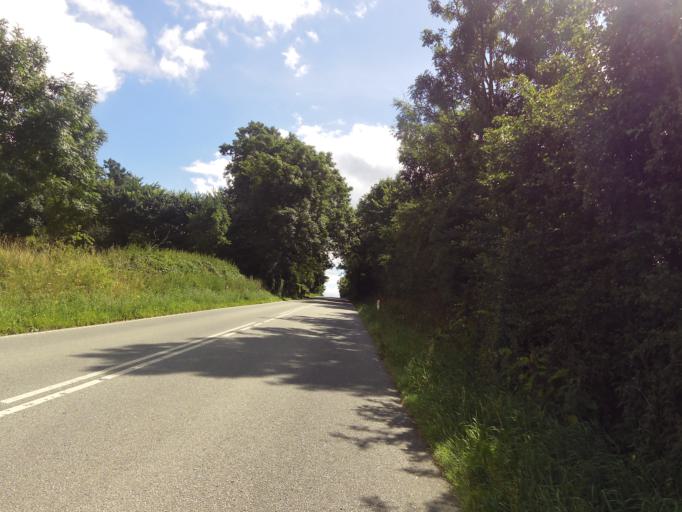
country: DK
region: South Denmark
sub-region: Haderslev Kommune
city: Haderslev
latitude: 55.2643
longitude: 9.4356
